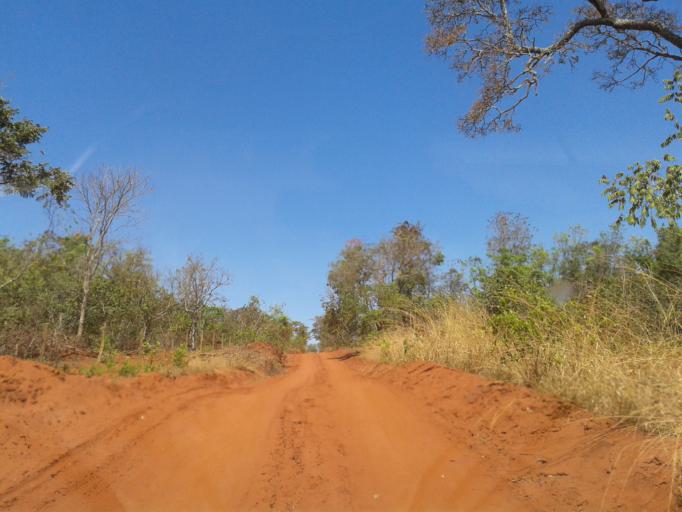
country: BR
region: Minas Gerais
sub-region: Ituiutaba
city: Ituiutaba
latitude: -19.0949
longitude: -49.2678
